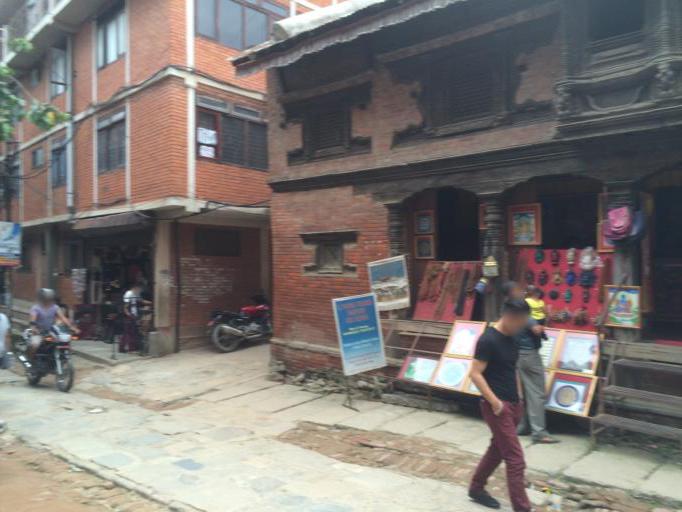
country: NP
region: Central Region
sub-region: Bagmati Zone
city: Patan
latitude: 27.6757
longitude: 85.3251
